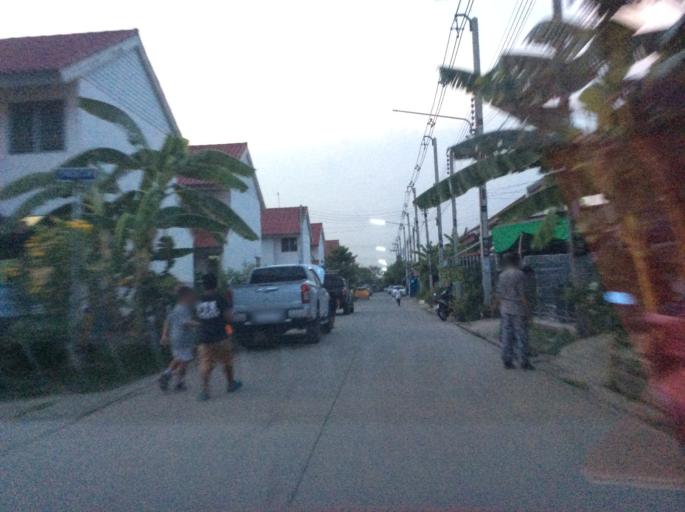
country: TH
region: Pathum Thani
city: Ban Rangsit
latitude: 14.0453
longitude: 100.7627
